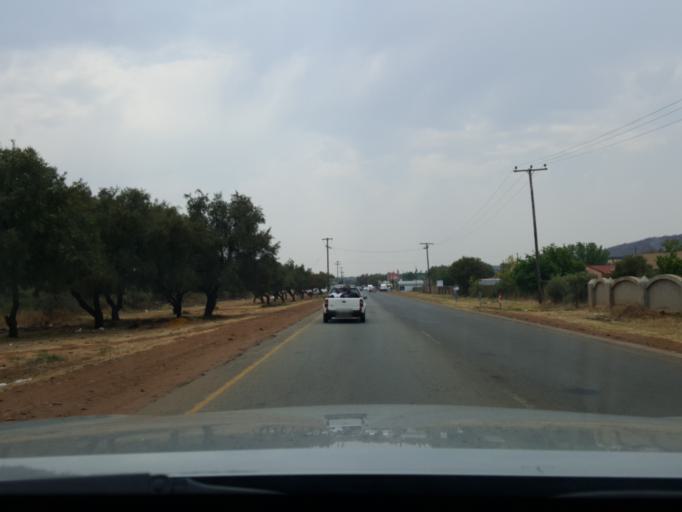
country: ZA
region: North-West
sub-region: Ngaka Modiri Molema District Municipality
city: Zeerust
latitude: -25.4966
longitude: 25.9841
